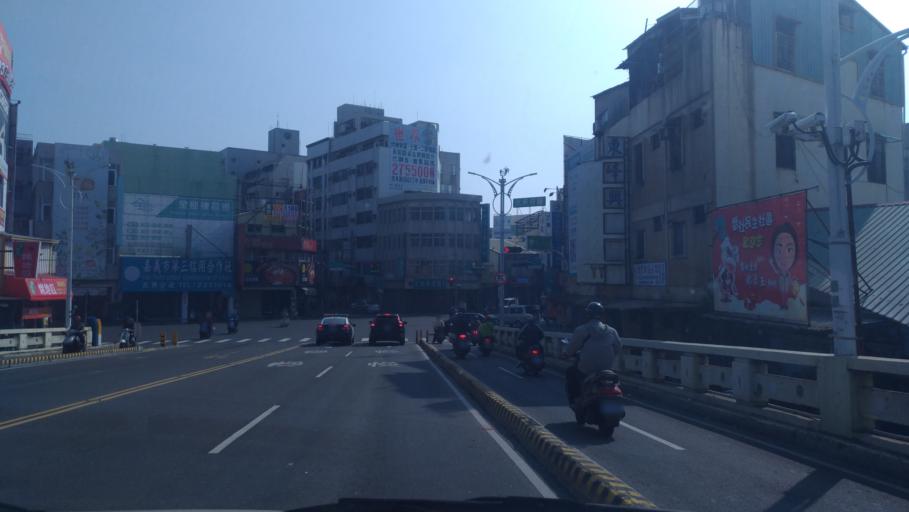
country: TW
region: Taiwan
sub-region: Chiayi
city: Jiayi Shi
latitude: 23.4822
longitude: 120.4453
